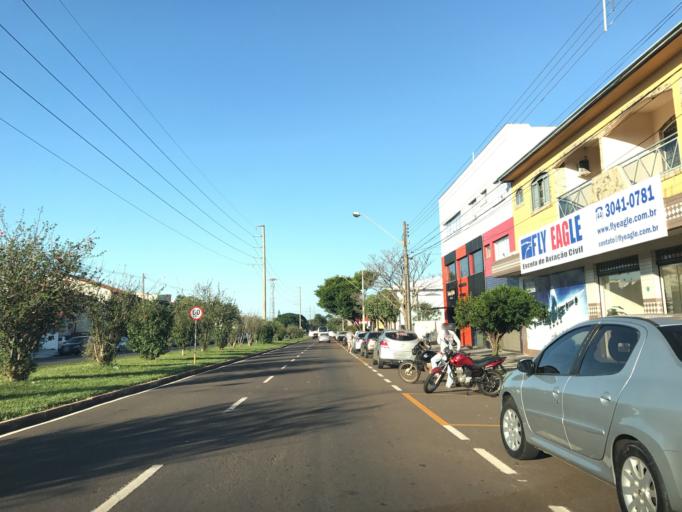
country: BR
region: Parana
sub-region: Maringa
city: Maringa
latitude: -23.4498
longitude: -51.9569
